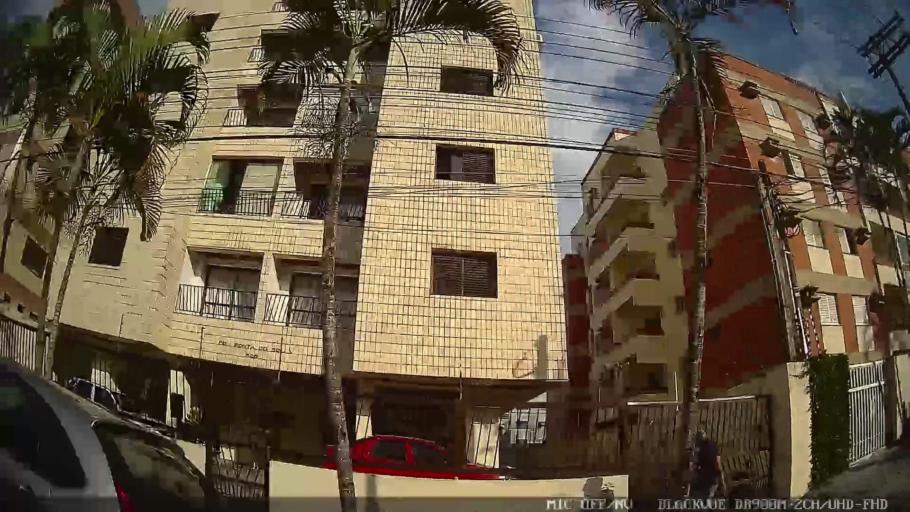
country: BR
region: Sao Paulo
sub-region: Guaruja
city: Guaruja
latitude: -23.9822
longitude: -46.2370
